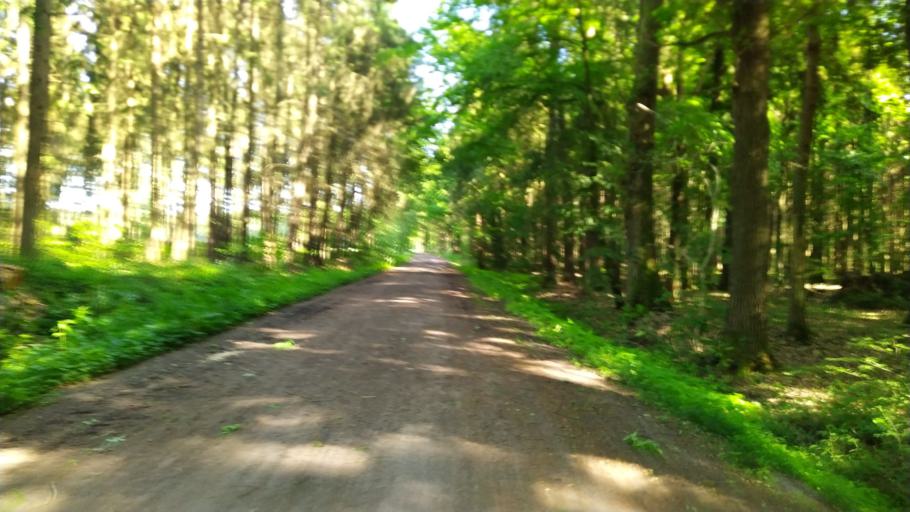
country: DE
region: Lower Saxony
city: Ahlerstedt
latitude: 53.4237
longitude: 9.4772
